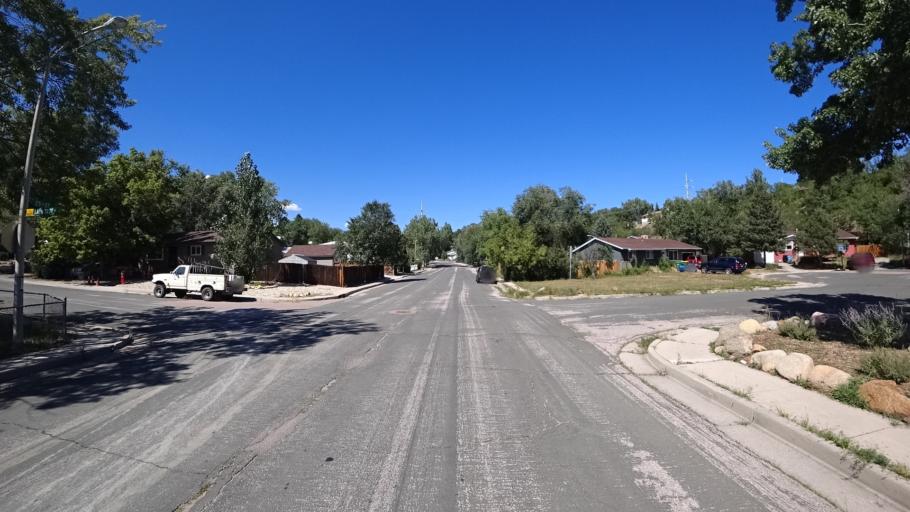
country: US
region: Colorado
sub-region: El Paso County
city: Colorado Springs
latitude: 38.8571
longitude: -104.8567
